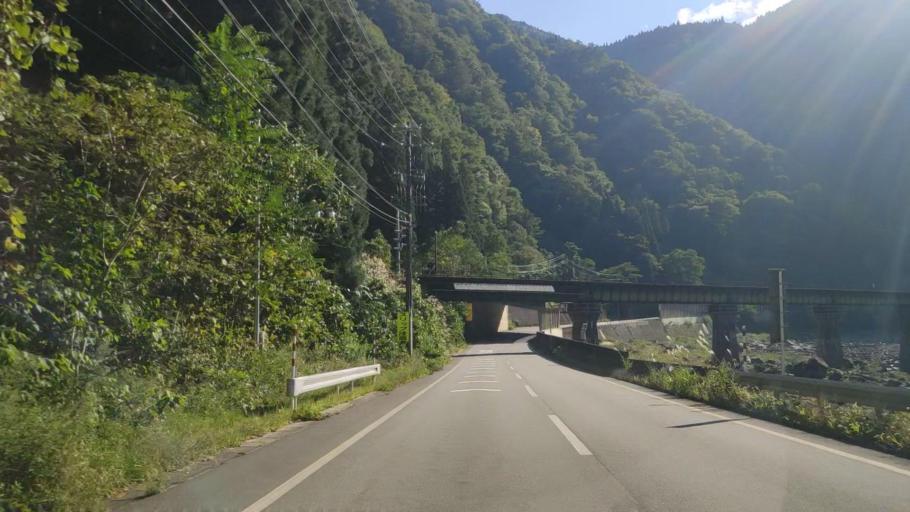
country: JP
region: Gifu
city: Takayama
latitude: 36.3134
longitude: 137.1310
